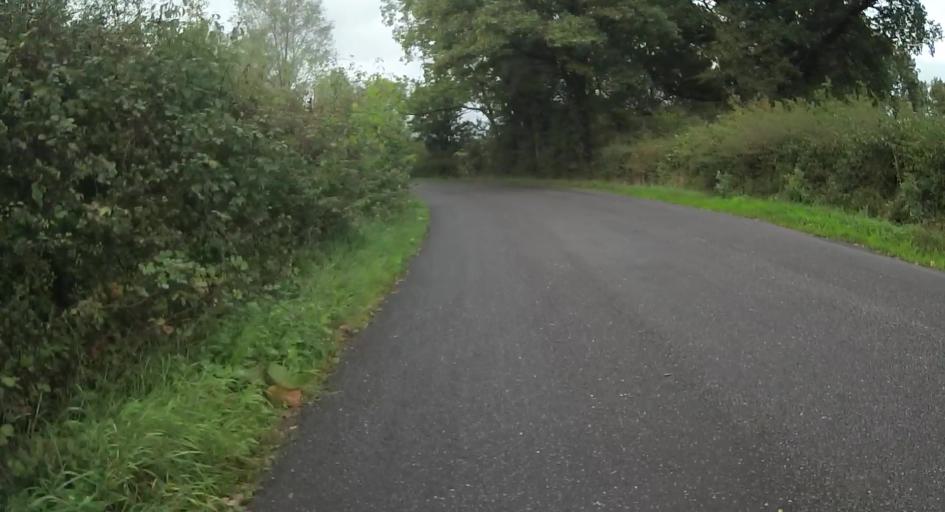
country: GB
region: England
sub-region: Hampshire
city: Tadley
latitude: 51.3064
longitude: -1.1523
